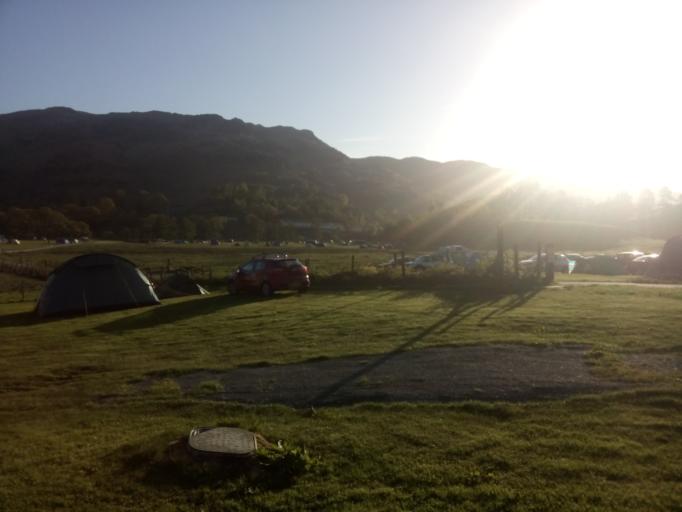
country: GB
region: England
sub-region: Cumbria
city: Ambleside
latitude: 54.4360
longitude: -3.0599
